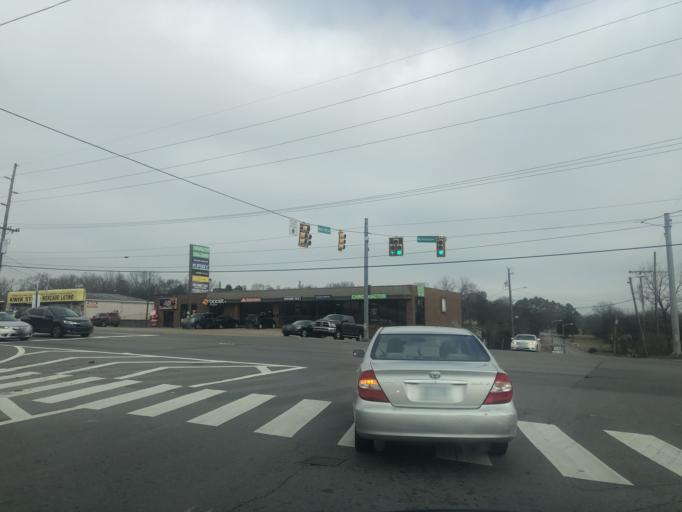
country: US
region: Tennessee
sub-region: Rutherford County
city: La Vergne
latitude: 36.0743
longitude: -86.6388
